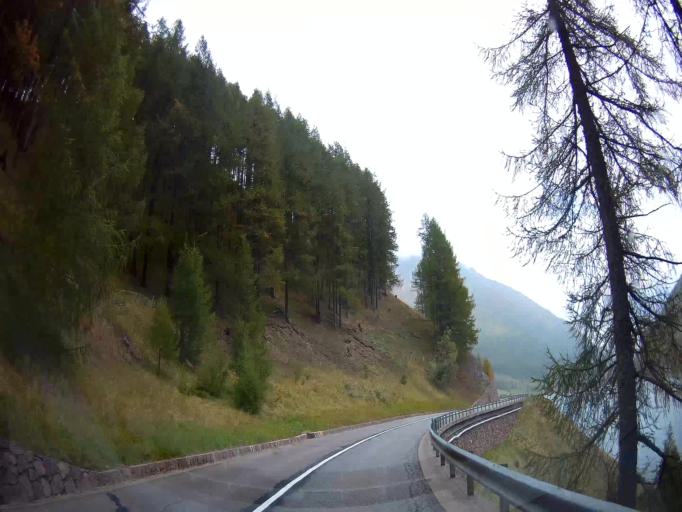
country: IT
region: Trentino-Alto Adige
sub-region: Bolzano
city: Senales
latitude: 46.7384
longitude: 10.8334
